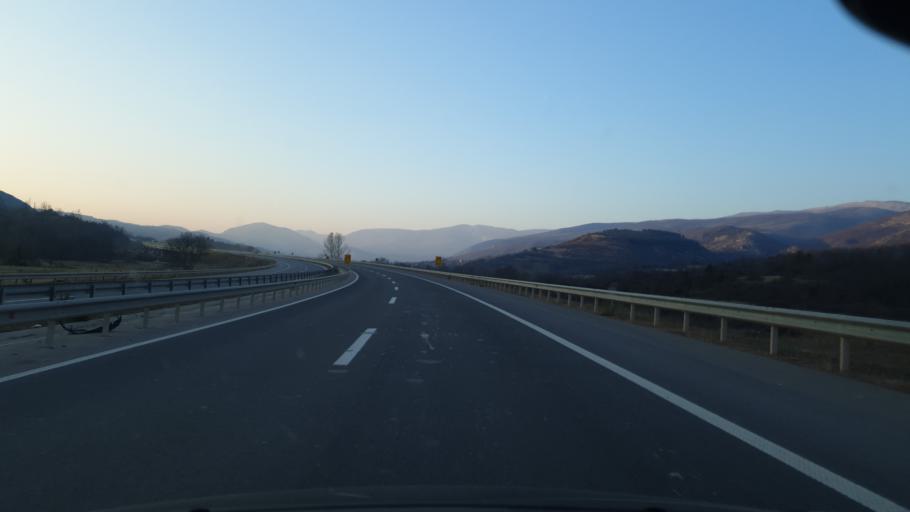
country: RS
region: Central Serbia
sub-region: Pirotski Okrug
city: Bela Palanka
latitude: 43.2557
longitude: 22.2674
